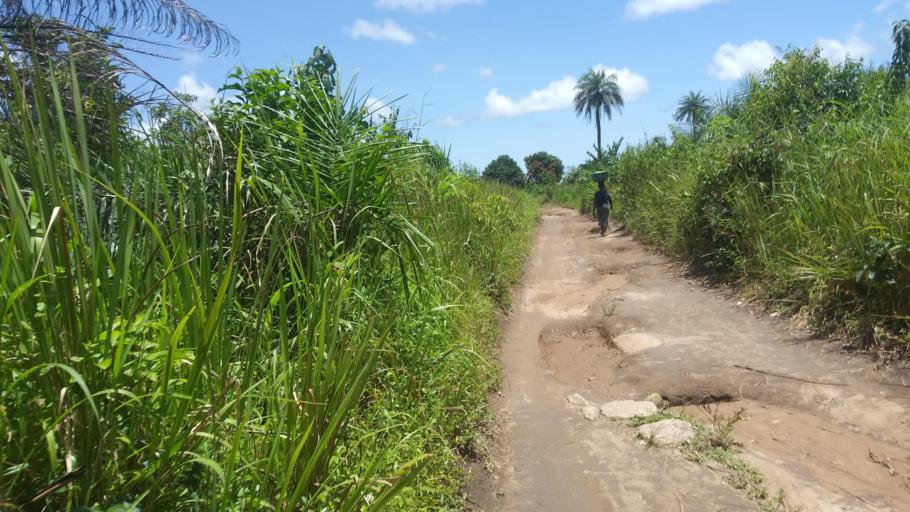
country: SL
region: Northern Province
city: Makeni
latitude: 8.8867
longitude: -12.0156
